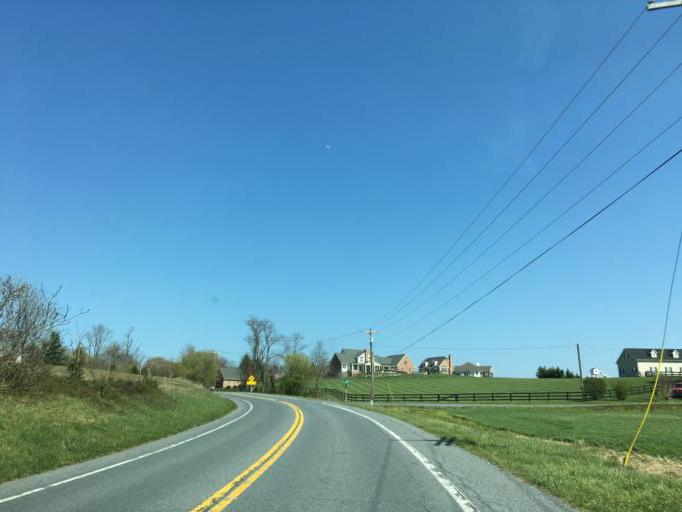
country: US
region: Maryland
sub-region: Carroll County
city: New Windsor
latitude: 39.4911
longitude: -77.1576
